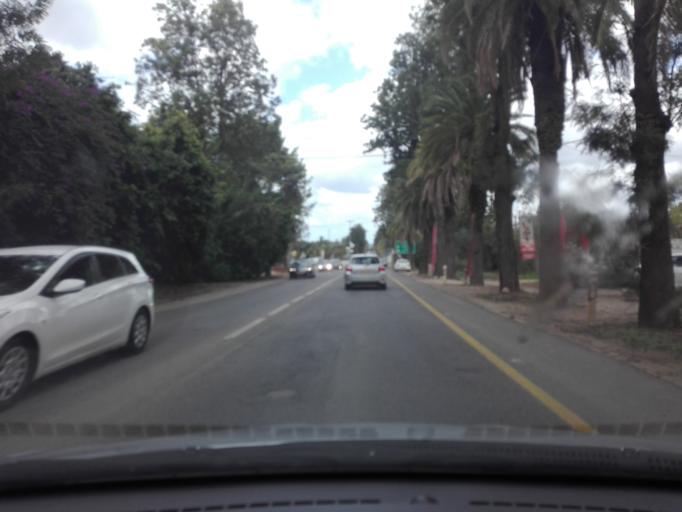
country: IL
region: Haifa
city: Qesarya
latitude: 32.4799
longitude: 34.9740
